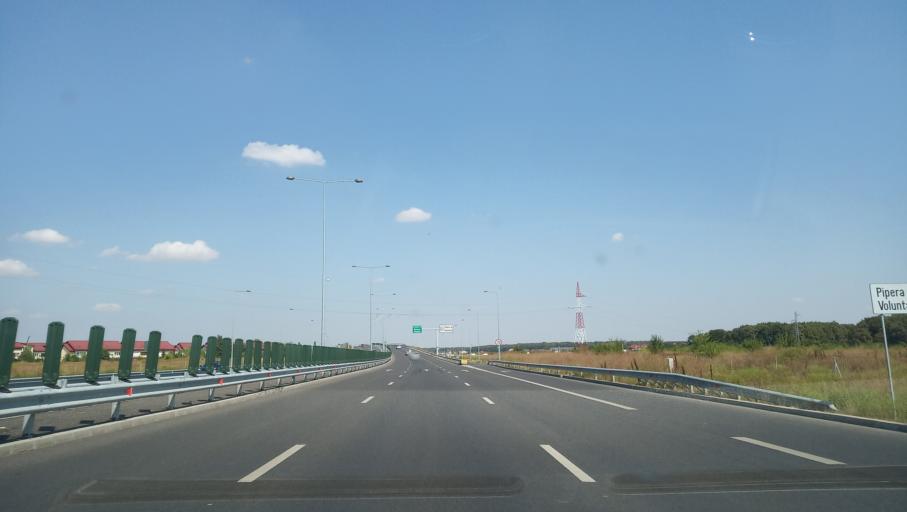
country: RO
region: Ilfov
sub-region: Voluntari City
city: Voluntari
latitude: 44.4888
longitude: 26.1459
